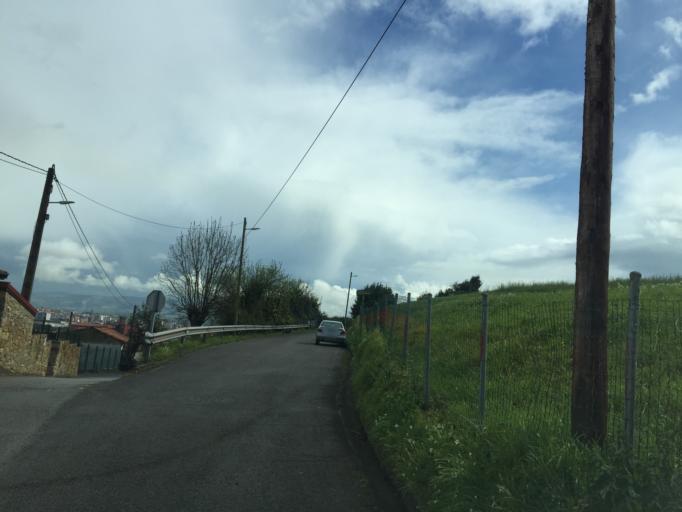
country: ES
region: Asturias
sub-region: Province of Asturias
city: Natahoyo
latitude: 43.5538
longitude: -5.7080
